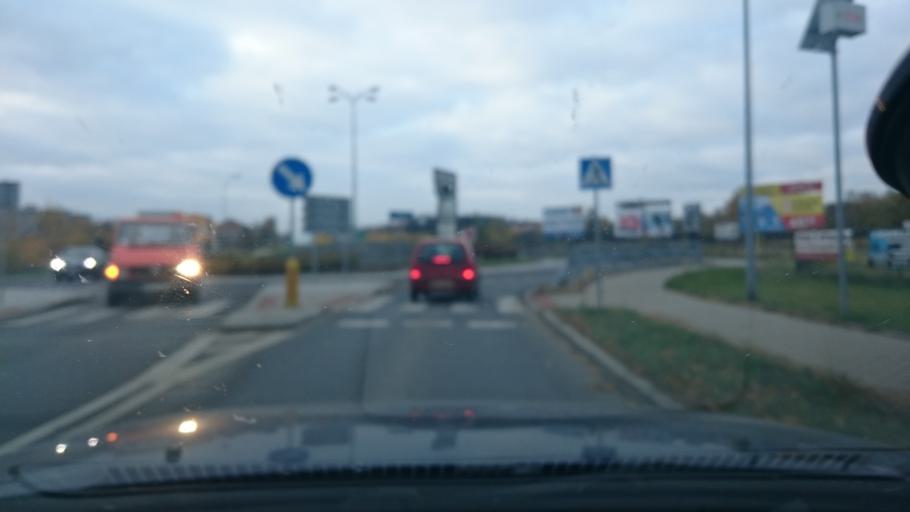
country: PL
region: Silesian Voivodeship
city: Zebrzydowice
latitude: 50.1156
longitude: 18.5155
